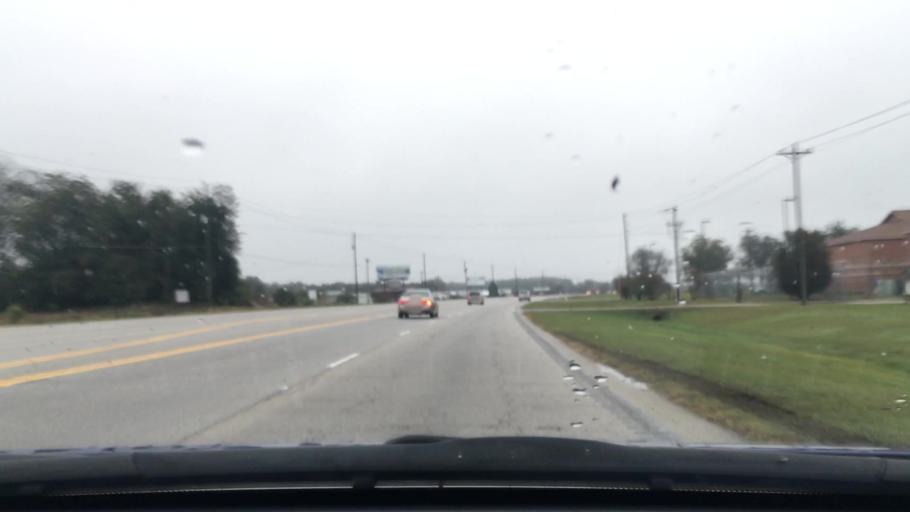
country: US
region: South Carolina
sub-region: Darlington County
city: Darlington
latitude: 34.3000
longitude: -79.9244
